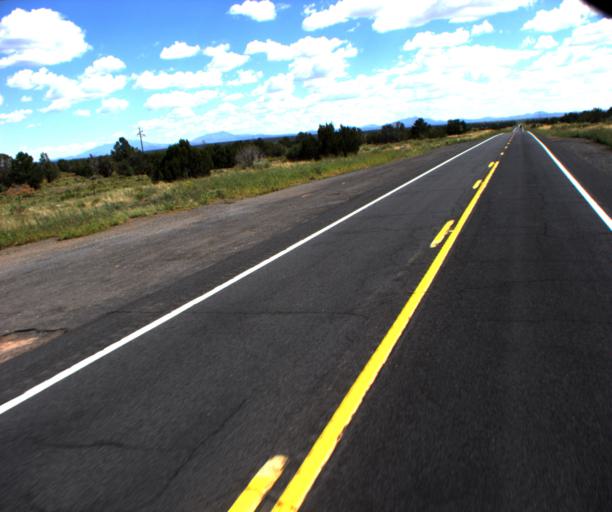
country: US
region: Arizona
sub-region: Coconino County
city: Grand Canyon Village
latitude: 35.8030
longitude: -112.1309
